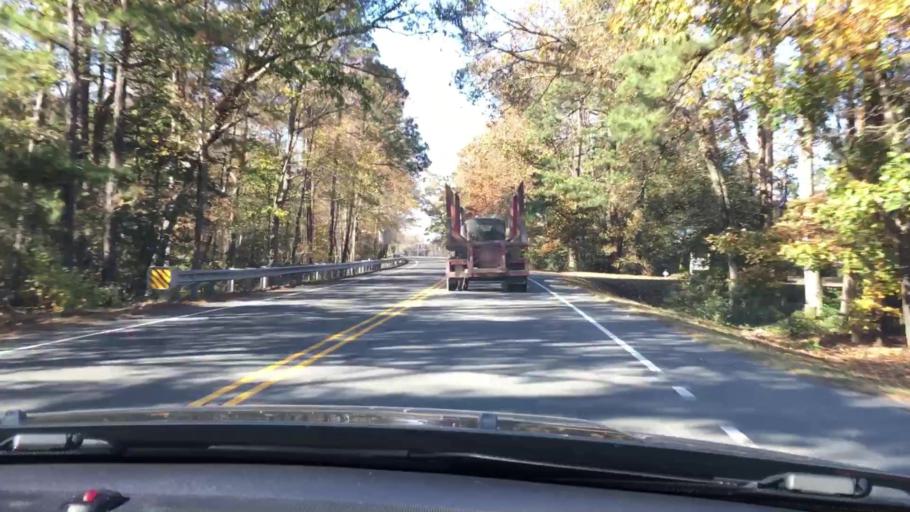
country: US
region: Virginia
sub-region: King William County
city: Central Garage
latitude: 37.7597
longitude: -77.1451
